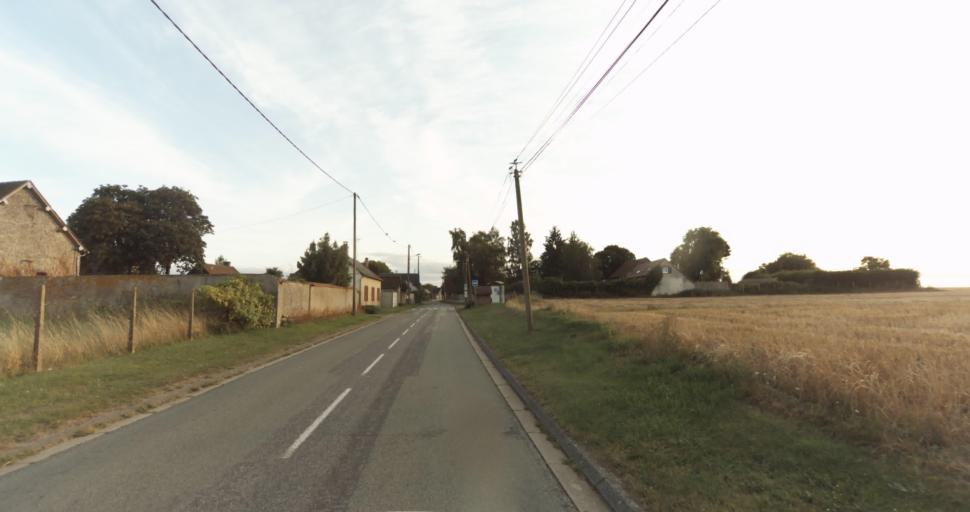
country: FR
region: Haute-Normandie
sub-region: Departement de l'Eure
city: Marcilly-sur-Eure
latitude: 48.8753
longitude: 1.2601
